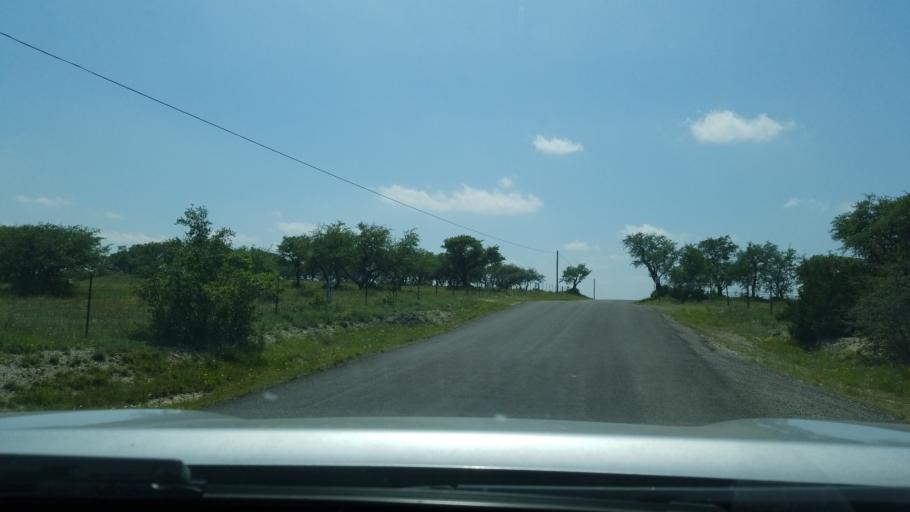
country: US
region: Texas
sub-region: Blanco County
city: Blanco
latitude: 29.9923
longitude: -98.5221
